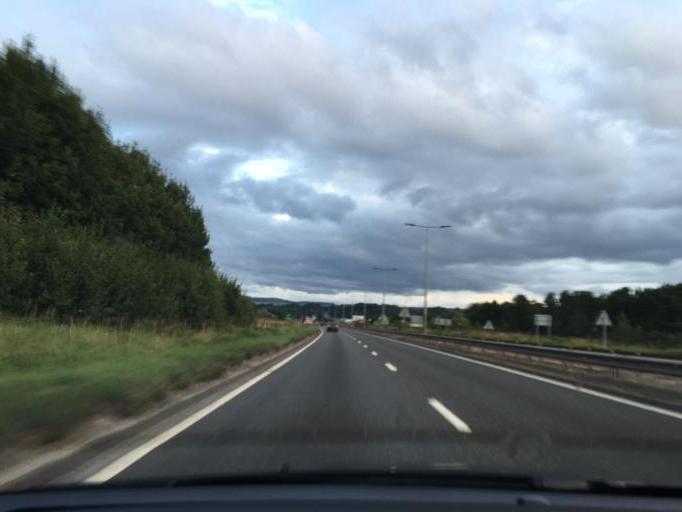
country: GB
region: Scotland
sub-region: Highland
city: Inverness
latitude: 57.4892
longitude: -4.2109
